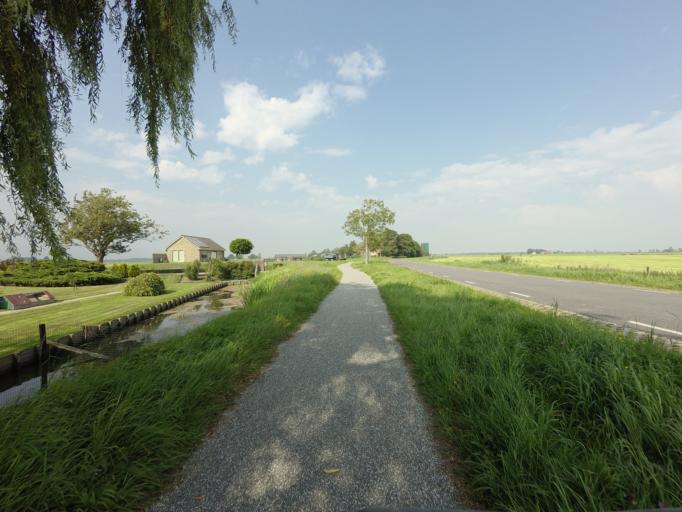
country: NL
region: Friesland
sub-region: Sudwest Fryslan
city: Bolsward
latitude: 53.0316
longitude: 5.5416
